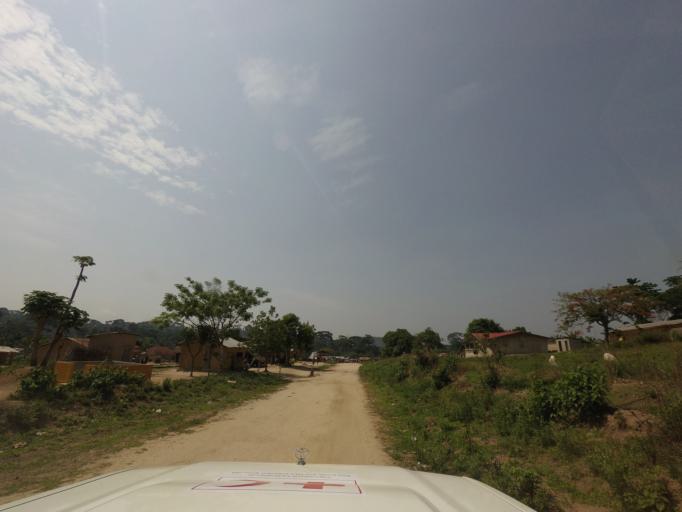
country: LR
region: Lofa
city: Voinjama
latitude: 8.5002
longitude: -9.6414
